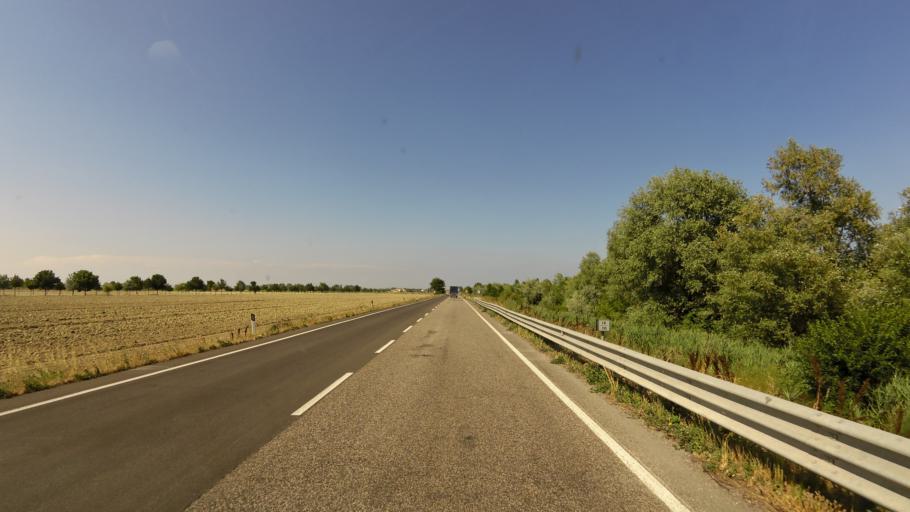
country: IT
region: Emilia-Romagna
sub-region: Provincia di Ravenna
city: Marina Romea
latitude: 44.5502
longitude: 12.2413
